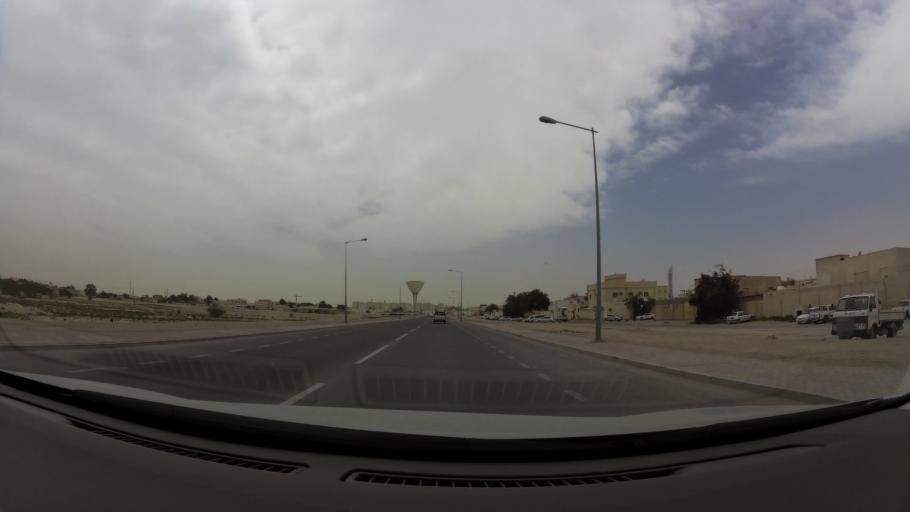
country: QA
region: Baladiyat ar Rayyan
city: Ar Rayyan
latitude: 25.2872
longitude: 51.4591
